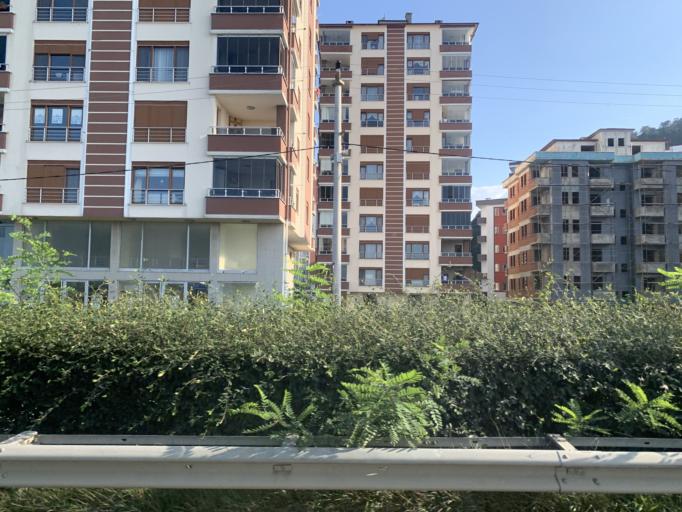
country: TR
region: Trabzon
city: Of
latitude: 40.9393
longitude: 40.2553
